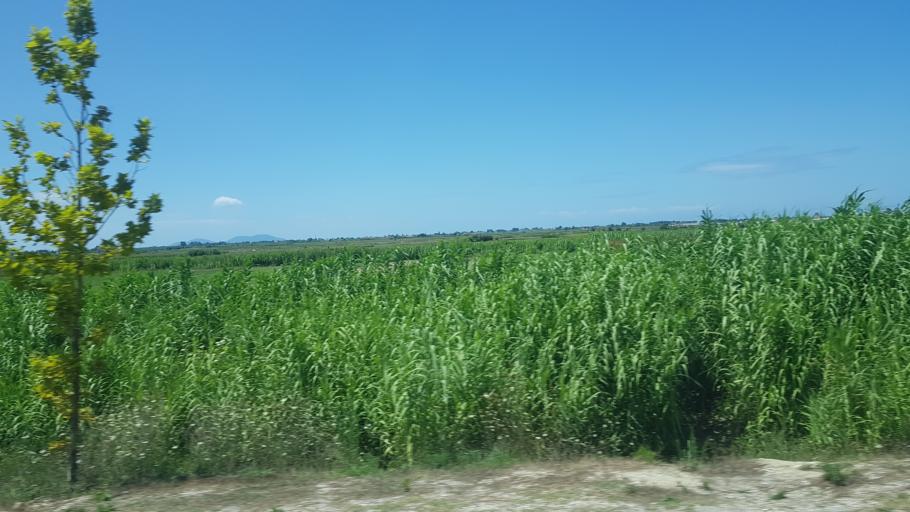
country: AL
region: Fier
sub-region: Rrethi i Fierit
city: Frakulla e Madhe
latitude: 40.6557
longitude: 19.4915
